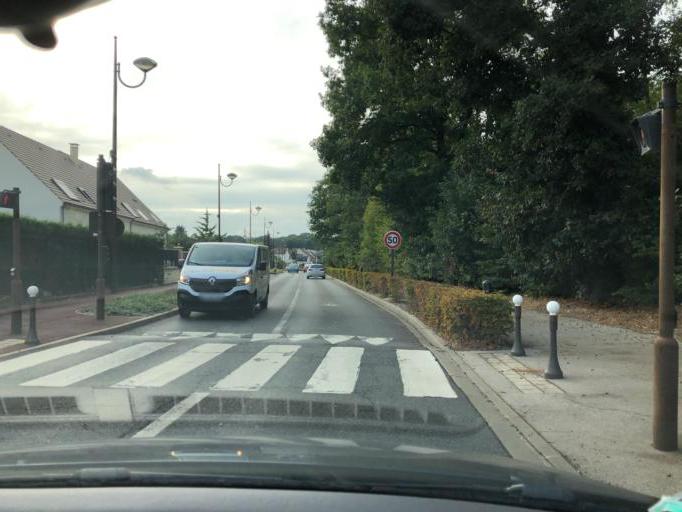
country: FR
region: Ile-de-France
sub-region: Departement des Yvelines
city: Velizy-Villacoublay
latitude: 48.7876
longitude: 2.1827
